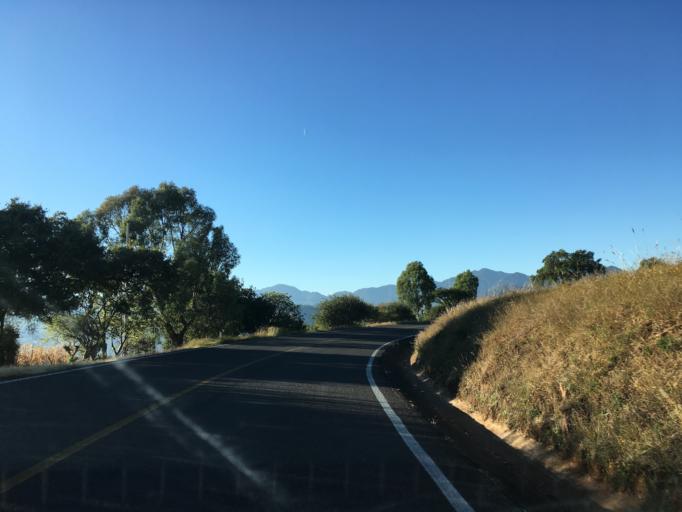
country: MX
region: Michoacan
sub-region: Tuxpan
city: La Soledad
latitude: 19.5024
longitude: -100.4642
